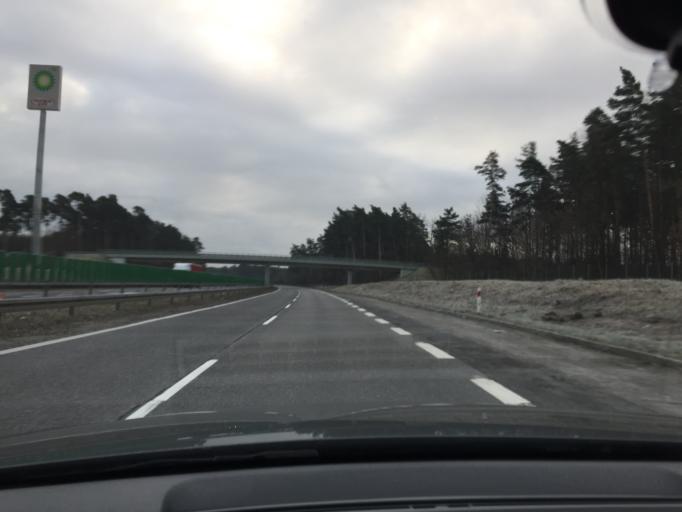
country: PL
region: Lubusz
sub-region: Powiat zarski
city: Trzebiel
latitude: 51.6484
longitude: 14.8280
